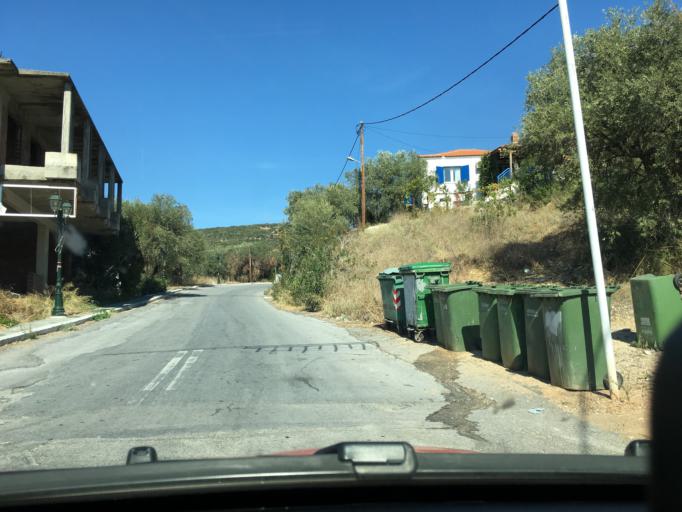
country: GR
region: Central Macedonia
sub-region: Nomos Chalkidikis
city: Agios Nikolaos
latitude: 40.3371
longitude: 23.7203
